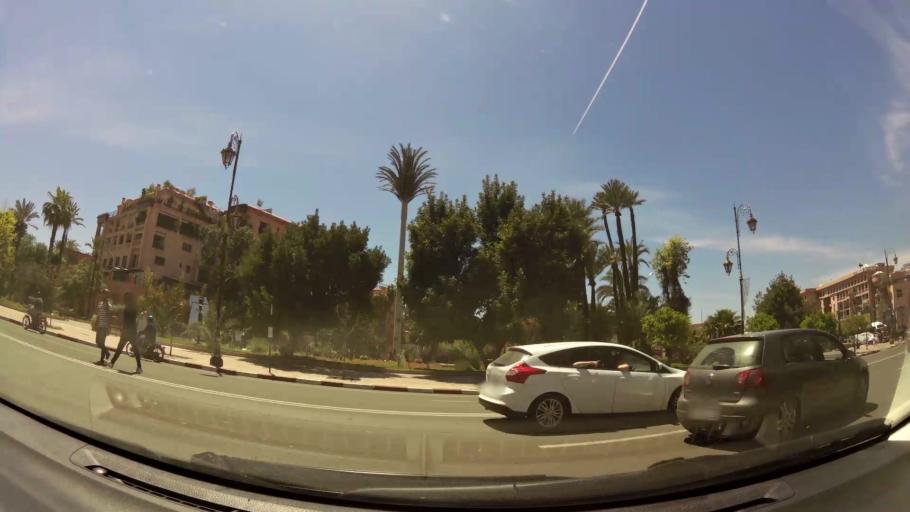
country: MA
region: Marrakech-Tensift-Al Haouz
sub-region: Marrakech
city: Marrakesh
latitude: 31.6294
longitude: -8.0028
